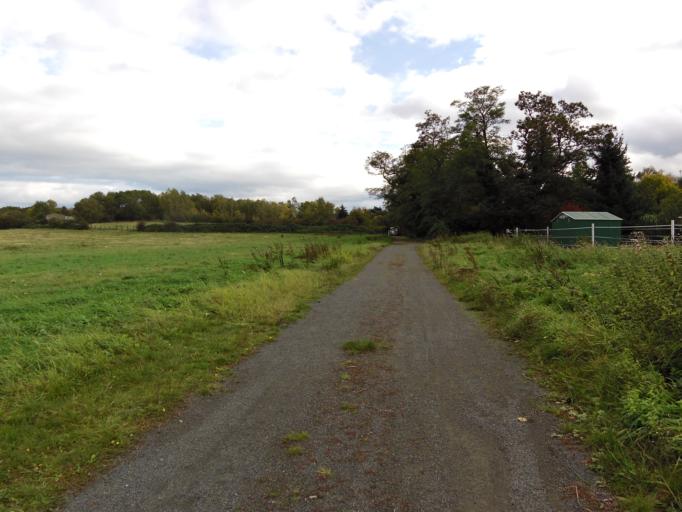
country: DE
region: Saxony
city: Grossposna
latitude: 51.2912
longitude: 12.4845
